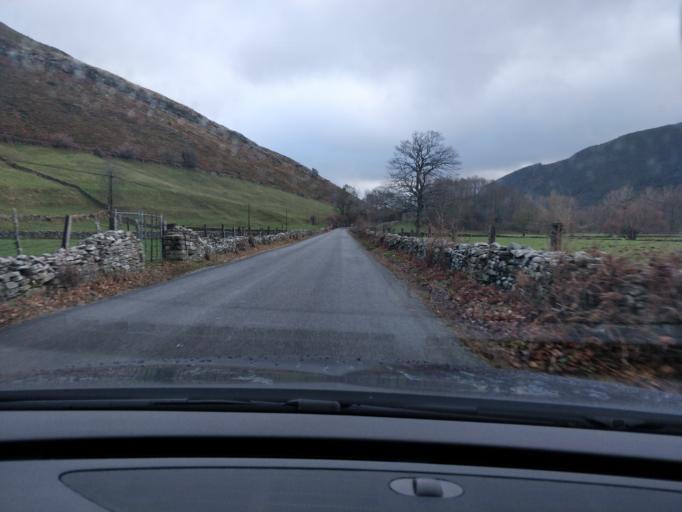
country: ES
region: Castille and Leon
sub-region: Provincia de Burgos
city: Espinosa de los Monteros
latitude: 43.1058
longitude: -3.5736
